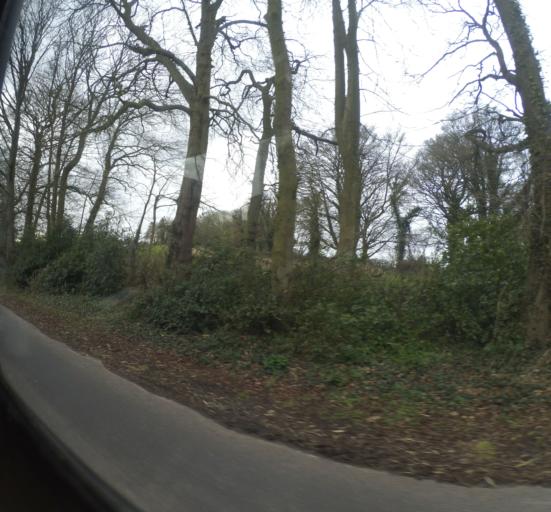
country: GB
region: England
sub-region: Warwickshire
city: Long Lawford
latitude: 52.4110
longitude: -1.3308
